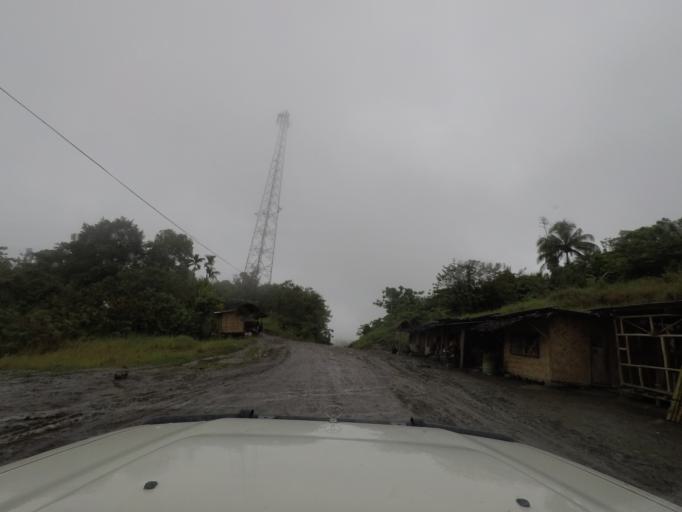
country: PG
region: Madang
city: Madang
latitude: -5.4684
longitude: 145.4859
